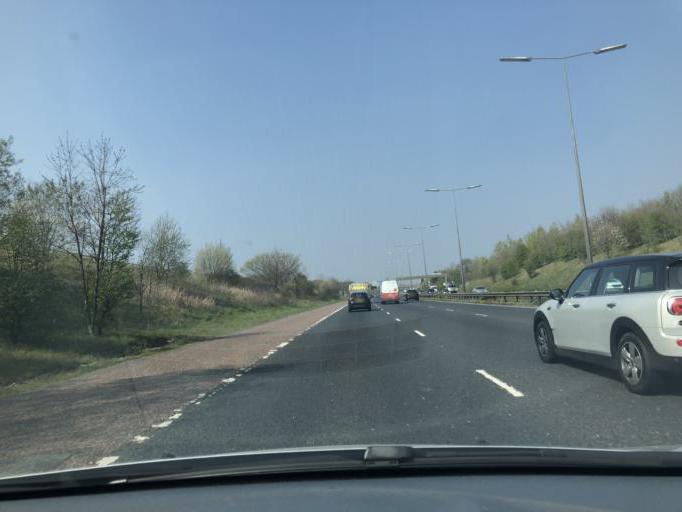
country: GB
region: England
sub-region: Borough of Tameside
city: Denton
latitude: 53.4446
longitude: -2.1336
